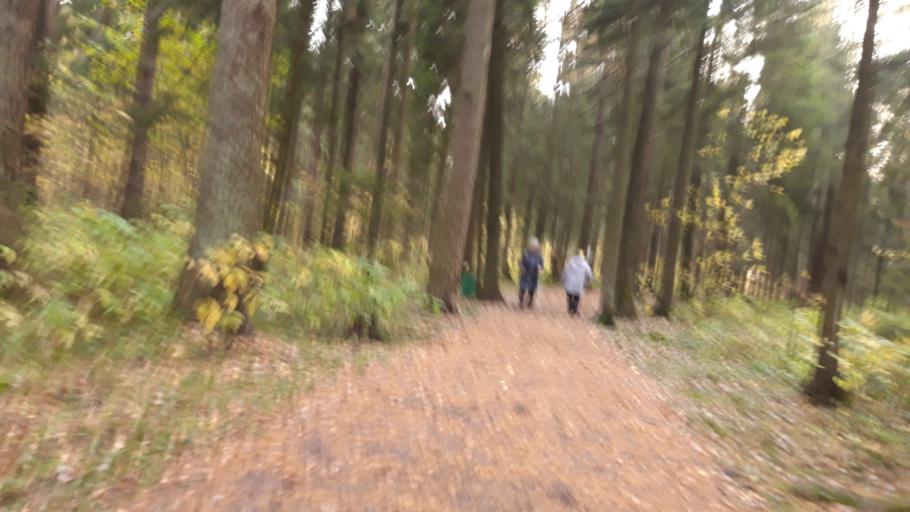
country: RU
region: Moscow
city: Zelenograd
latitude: 56.0008
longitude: 37.1789
